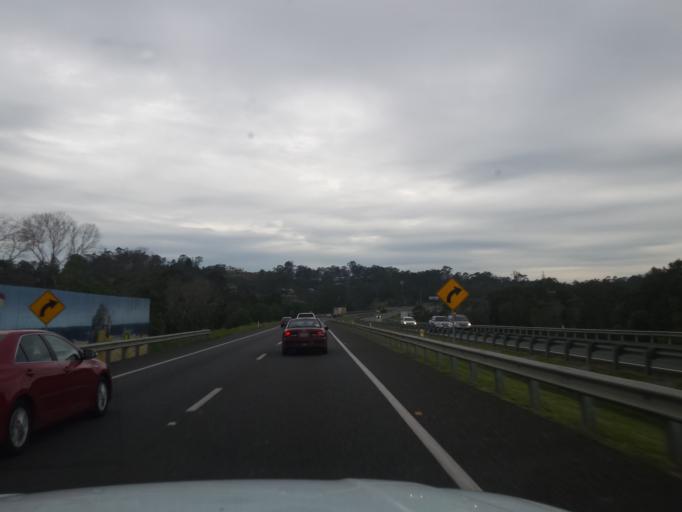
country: AU
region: Queensland
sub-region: Logan
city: Slacks Creek
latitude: -27.6668
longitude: 153.1570
